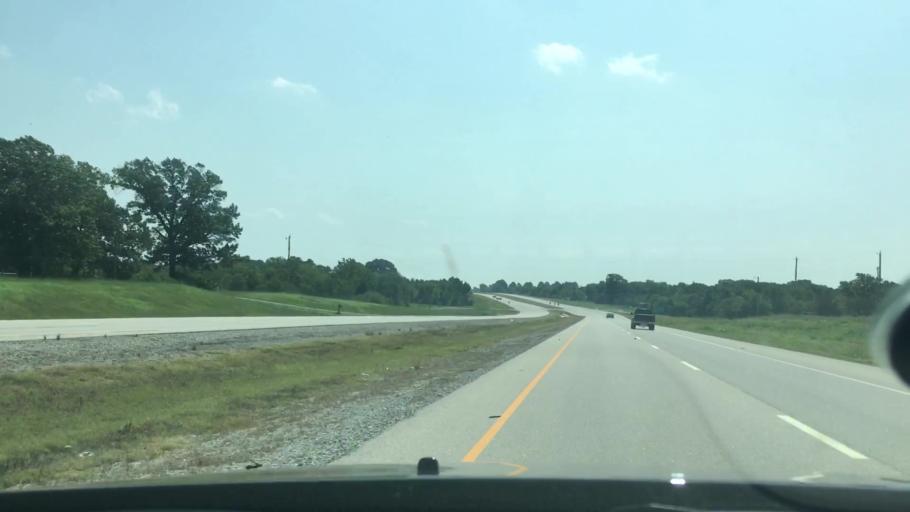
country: US
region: Oklahoma
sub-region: Atoka County
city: Atoka
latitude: 34.3476
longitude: -96.0780
